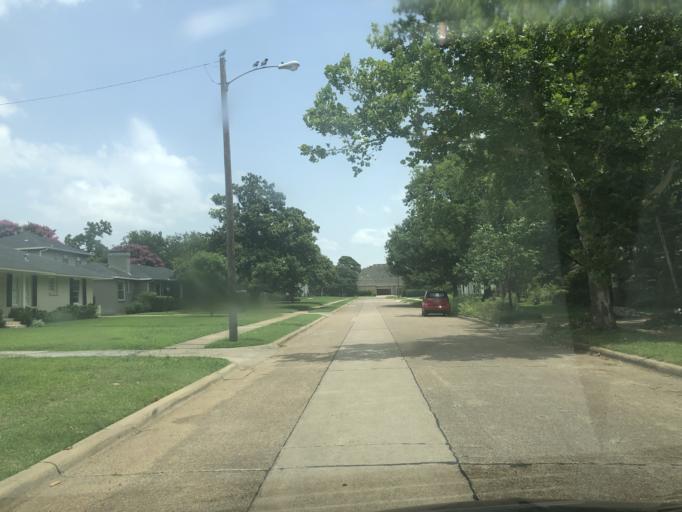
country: US
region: Texas
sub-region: Dallas County
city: University Park
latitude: 32.8698
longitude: -96.8470
